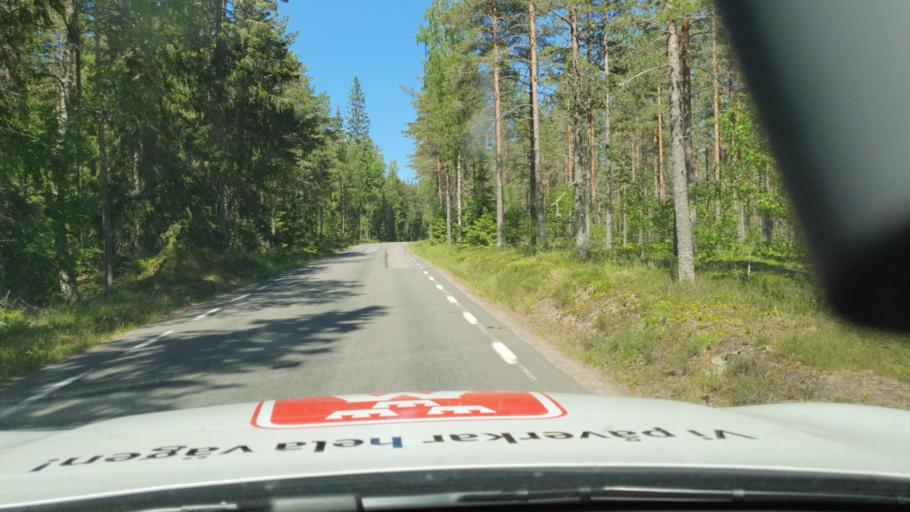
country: SE
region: Vaestra Goetaland
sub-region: Tidaholms Kommun
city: Tidaholm
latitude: 58.0695
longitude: 14.0657
